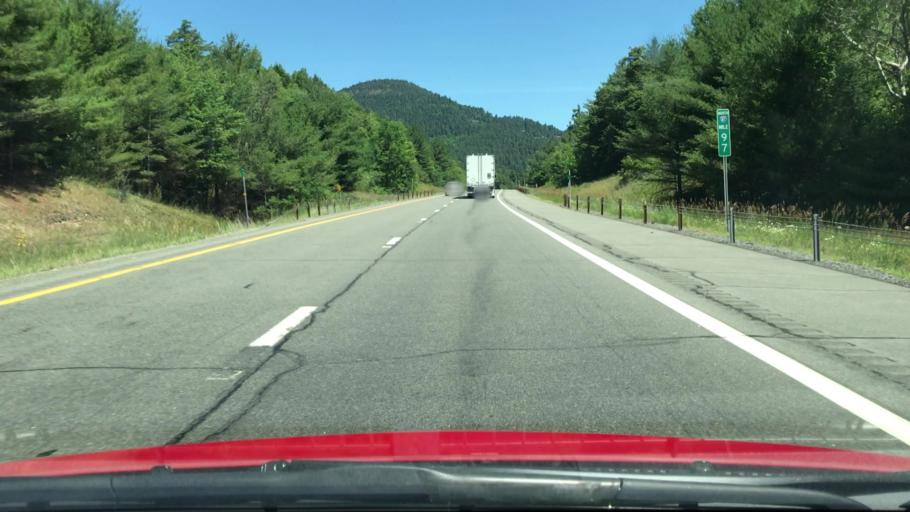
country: US
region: New York
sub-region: Essex County
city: Mineville
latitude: 43.9871
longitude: -73.7230
